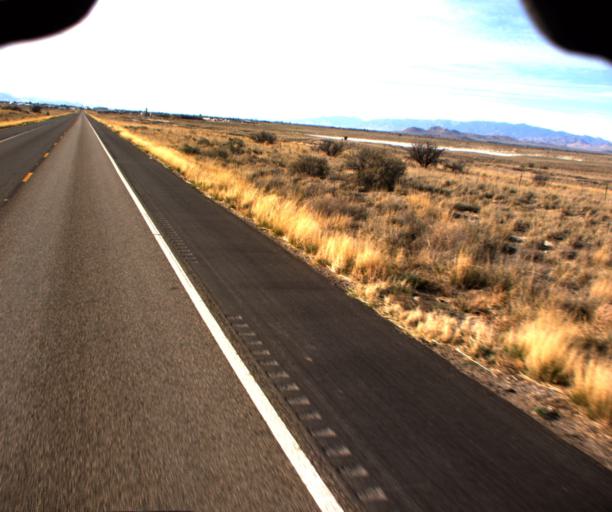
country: US
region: Arizona
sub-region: Cochise County
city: Willcox
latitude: 32.2318
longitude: -109.8027
